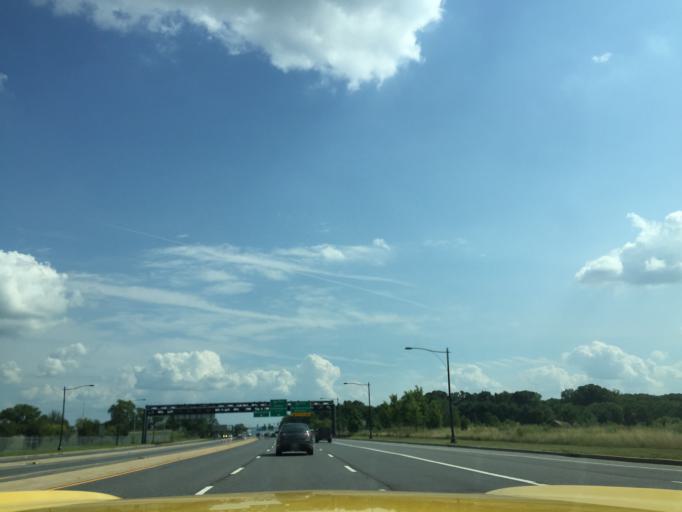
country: US
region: Delaware
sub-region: New Castle County
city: Wilmington
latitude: 39.7751
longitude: -75.5444
